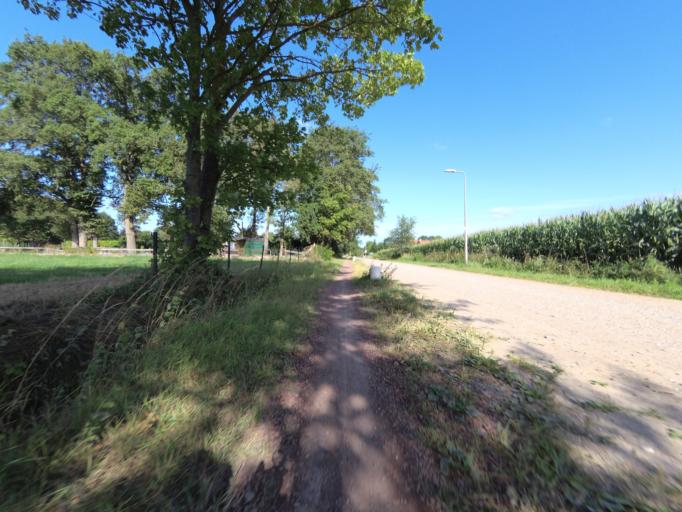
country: NL
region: Overijssel
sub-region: Gemeente Hengelo
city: Hengelo
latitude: 52.2477
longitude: 6.8168
